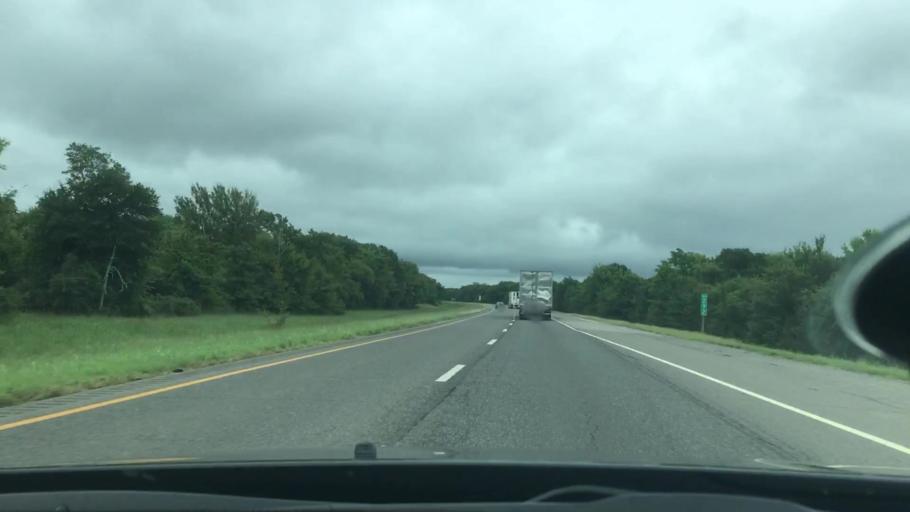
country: US
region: Oklahoma
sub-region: Sequoyah County
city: Vian
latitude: 35.4888
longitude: -95.0722
